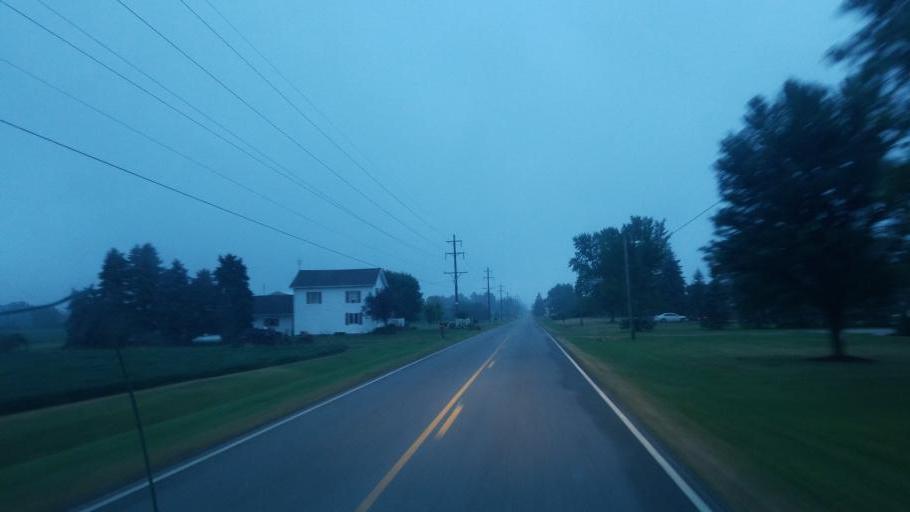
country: US
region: Ohio
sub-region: Defiance County
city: Hicksville
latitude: 41.3313
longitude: -84.7668
